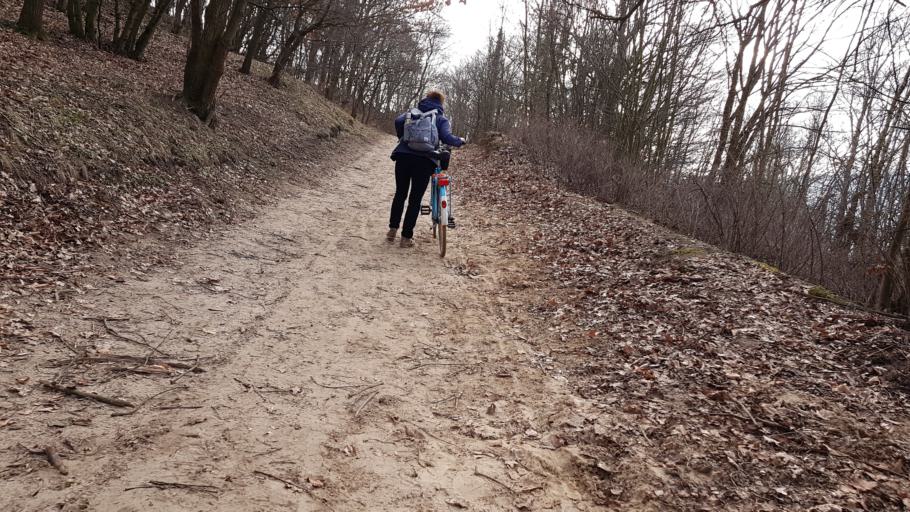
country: PL
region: West Pomeranian Voivodeship
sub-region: Powiat gryfinski
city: Gryfino
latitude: 53.2463
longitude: 14.4925
